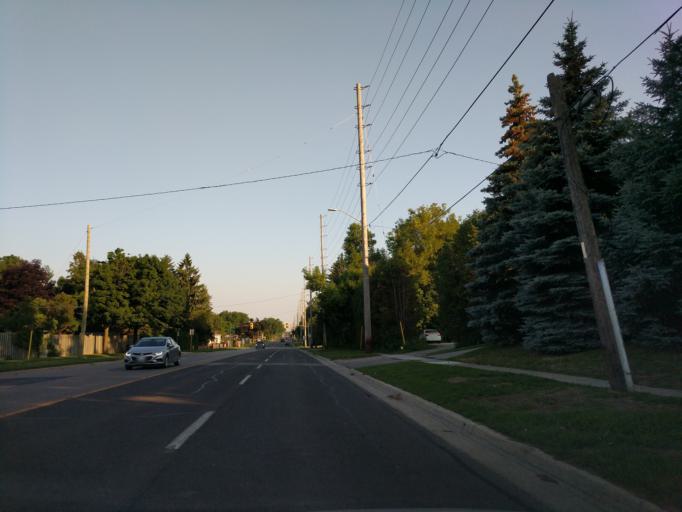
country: CA
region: Ontario
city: Oshawa
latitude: 43.9022
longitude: -78.8982
